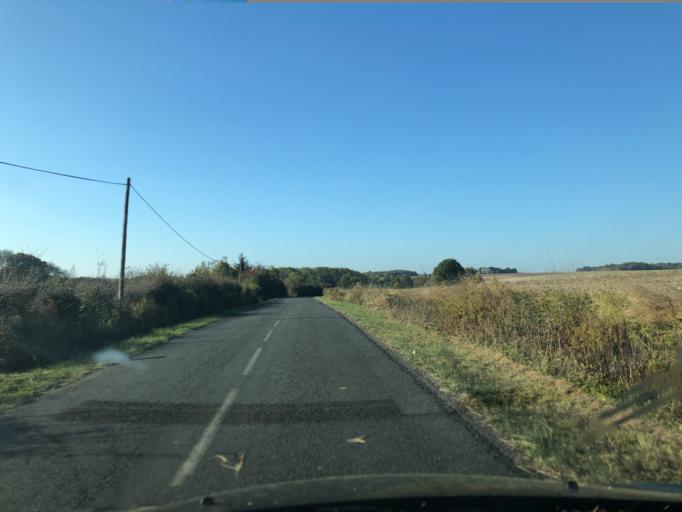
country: FR
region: Centre
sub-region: Departement d'Indre-et-Loire
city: Neuvy-le-Roi
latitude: 47.6610
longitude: 0.6389
